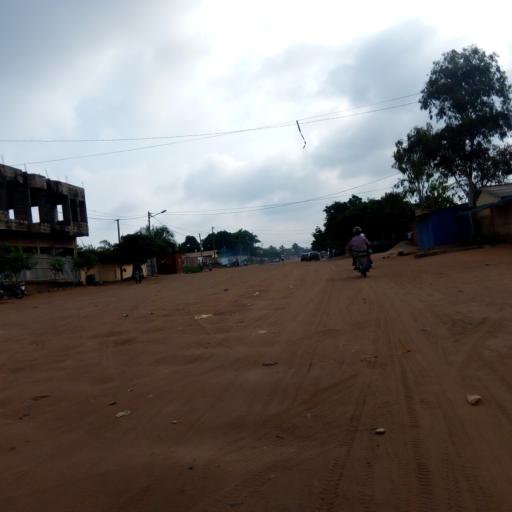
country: TG
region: Maritime
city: Lome
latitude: 6.1815
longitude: 1.1757
